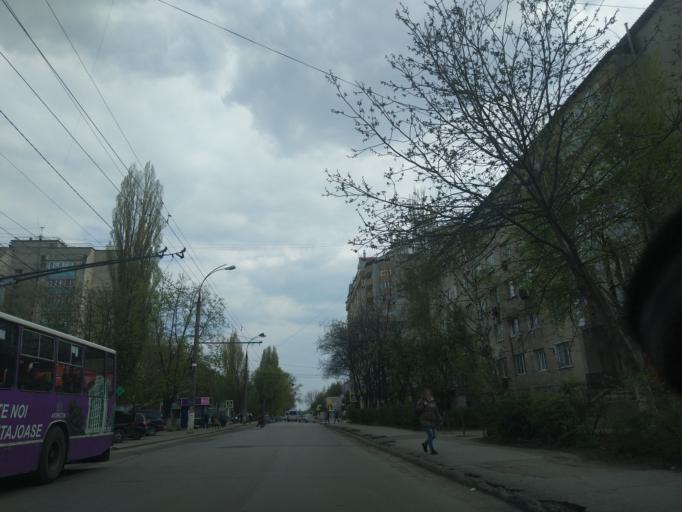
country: MD
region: Chisinau
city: Chisinau
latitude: 46.9869
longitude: 28.8730
